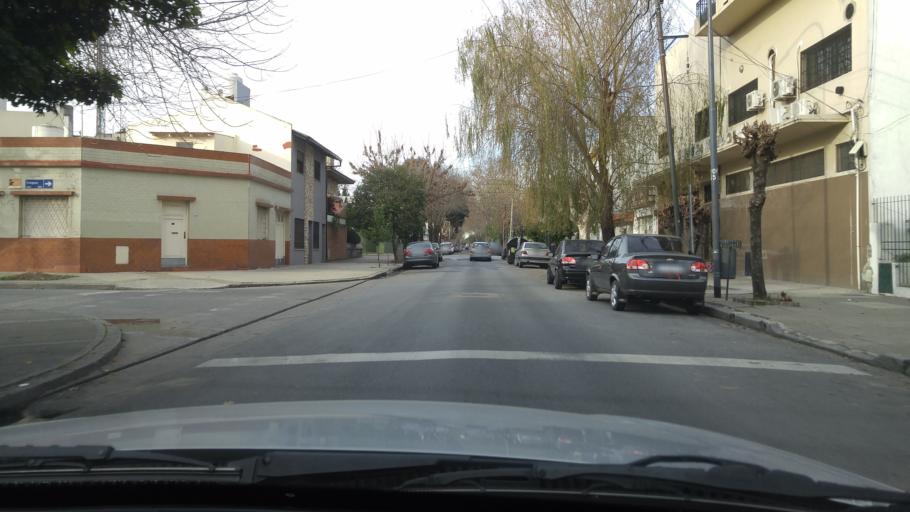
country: AR
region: Buenos Aires F.D.
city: Villa Santa Rita
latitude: -34.6301
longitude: -58.5251
